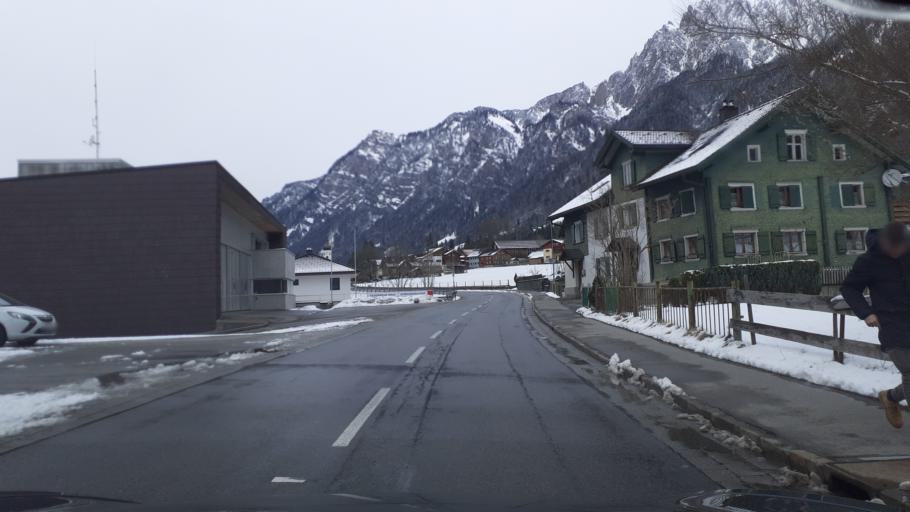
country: AT
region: Vorarlberg
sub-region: Politischer Bezirk Bludenz
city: Innerbraz
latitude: 47.1425
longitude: 9.9240
